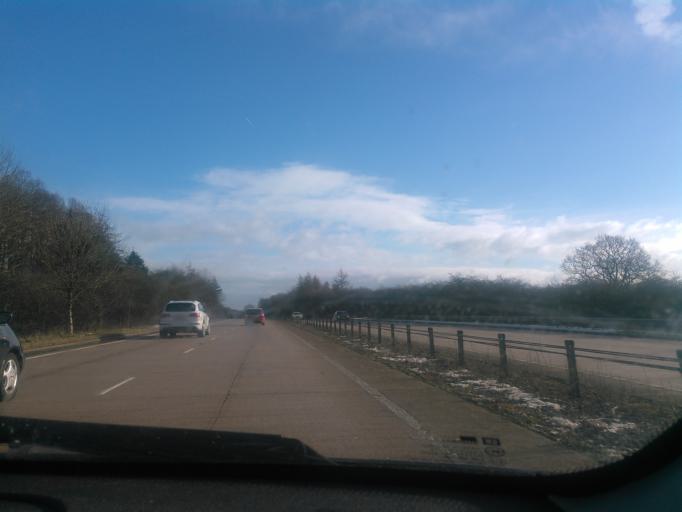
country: GB
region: England
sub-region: Staffordshire
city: Cheadle
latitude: 52.9346
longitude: -1.9739
